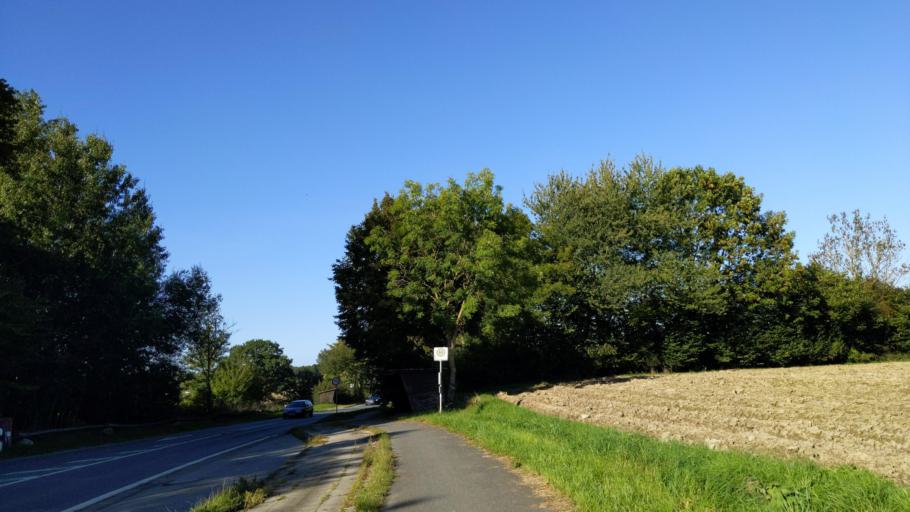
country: DE
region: Schleswig-Holstein
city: Ahrensbok
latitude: 53.9926
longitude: 10.5779
